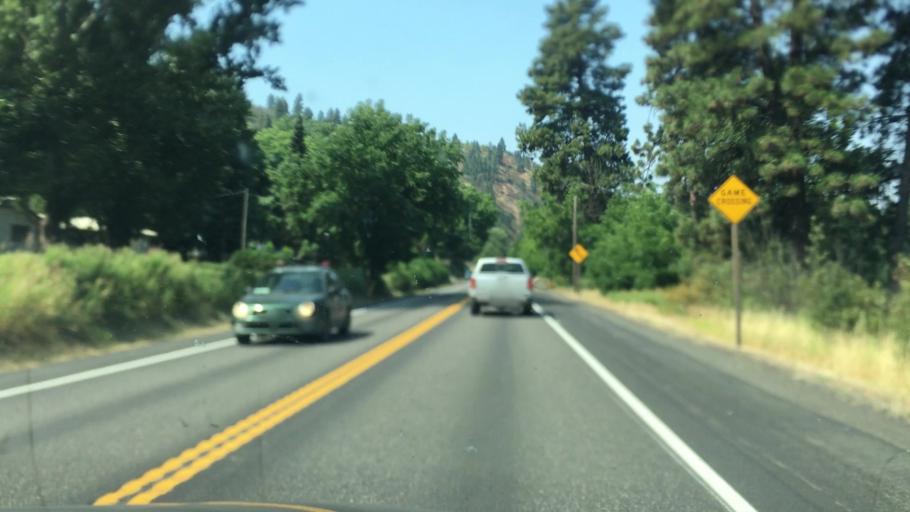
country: US
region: Idaho
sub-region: Clearwater County
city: Orofino
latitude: 46.5000
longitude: -116.4791
